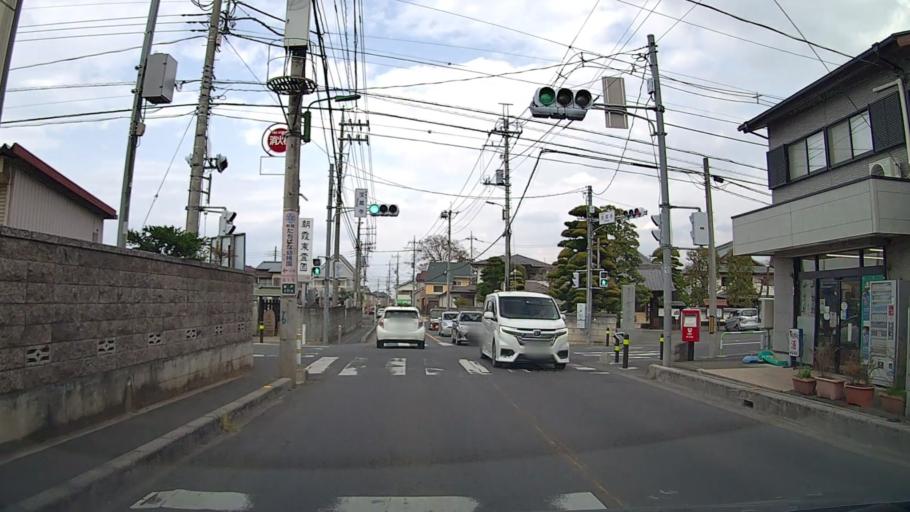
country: JP
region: Saitama
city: Shiki
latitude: 35.8263
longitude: 139.5891
